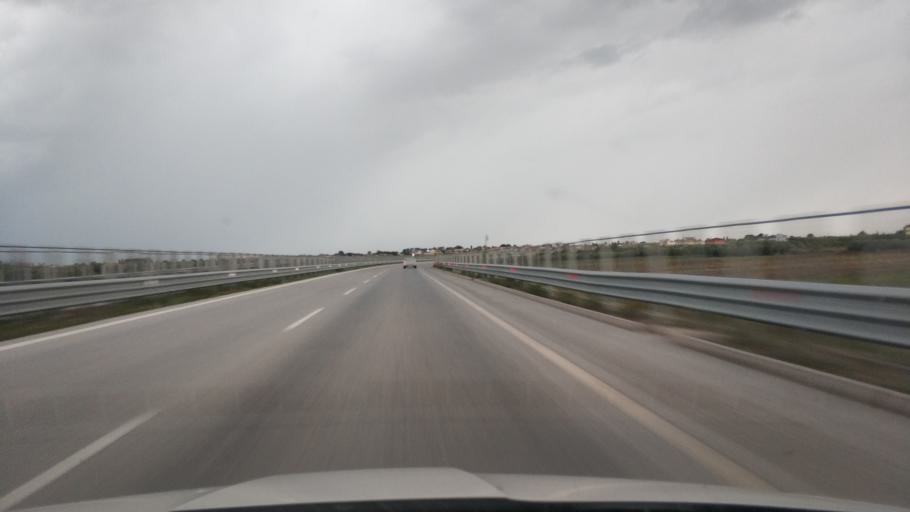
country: AL
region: Vlore
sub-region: Rrethi i Vlores
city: Novosele
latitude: 40.6305
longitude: 19.4487
